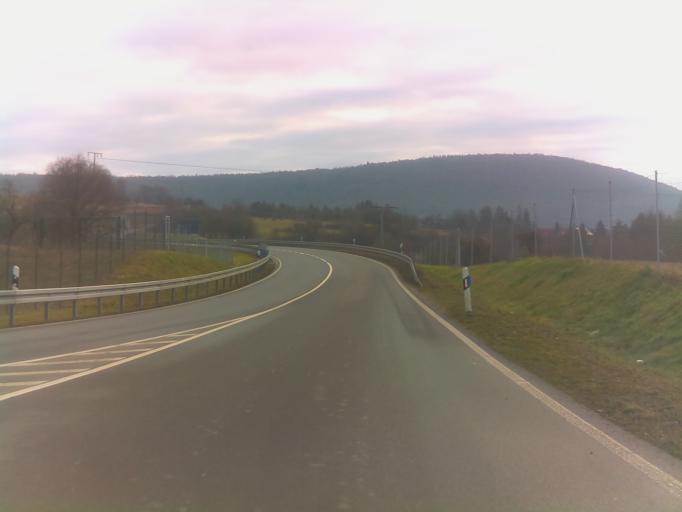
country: DE
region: Bavaria
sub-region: Regierungsbezirk Unterfranken
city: Faulbach
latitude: 49.7927
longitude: 9.4344
